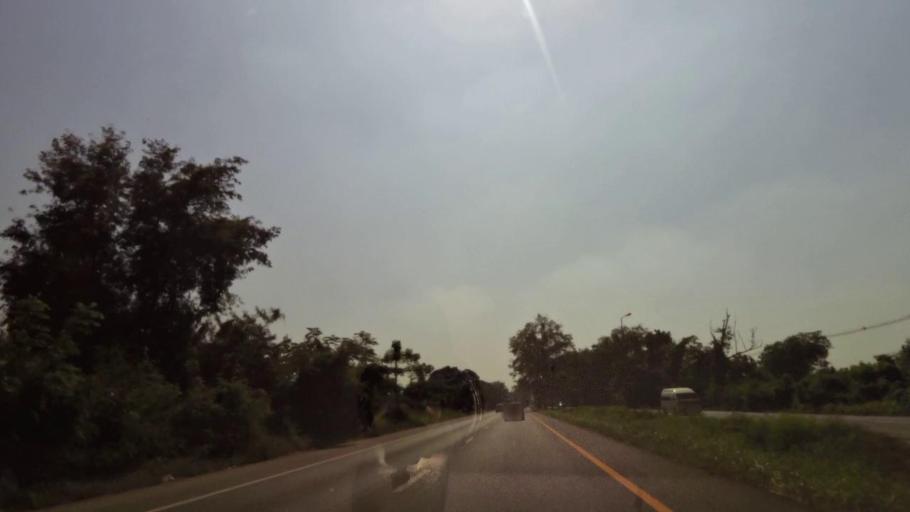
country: TH
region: Phichit
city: Bueng Na Rang
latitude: 16.0375
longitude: 100.1170
